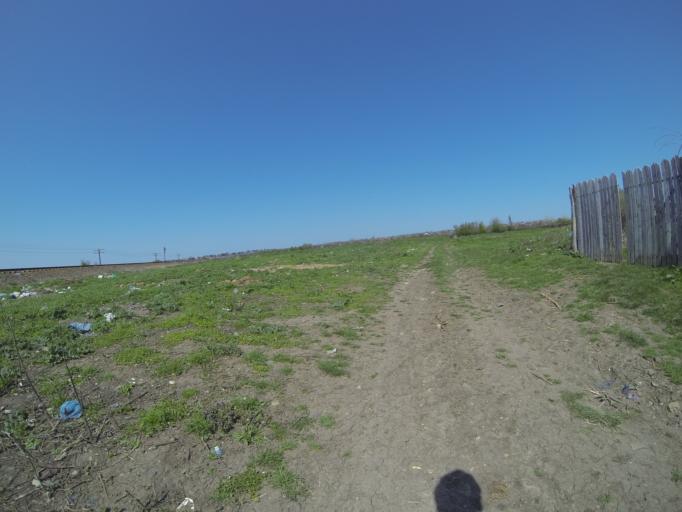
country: RO
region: Dolj
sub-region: Comuna Segarcea
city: Segarcea
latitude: 44.0926
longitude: 23.7284
